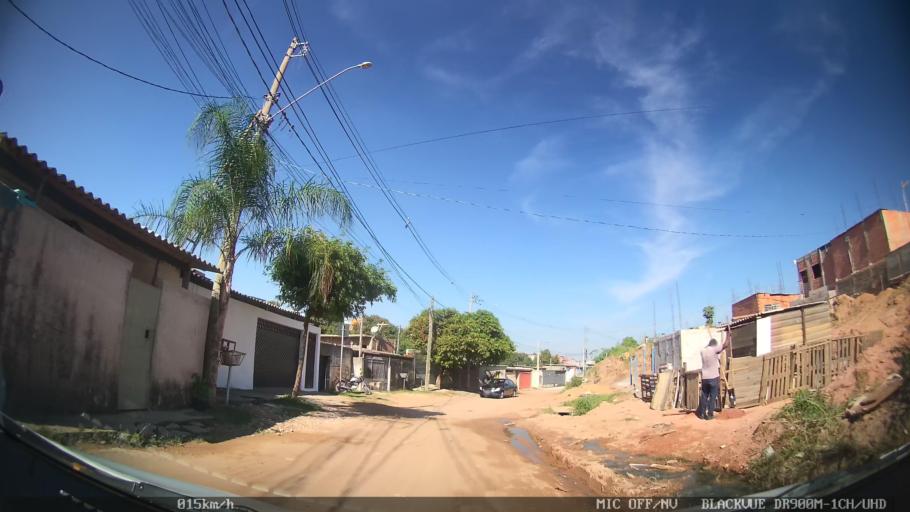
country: BR
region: Sao Paulo
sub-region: Campinas
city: Campinas
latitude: -22.9422
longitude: -47.0852
